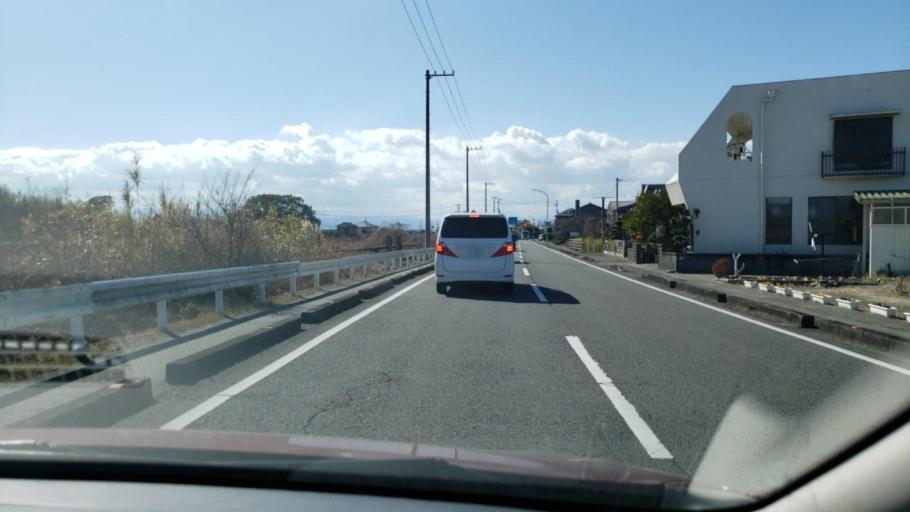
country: JP
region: Tokushima
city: Narutocho-mitsuishi
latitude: 34.1569
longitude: 134.5337
